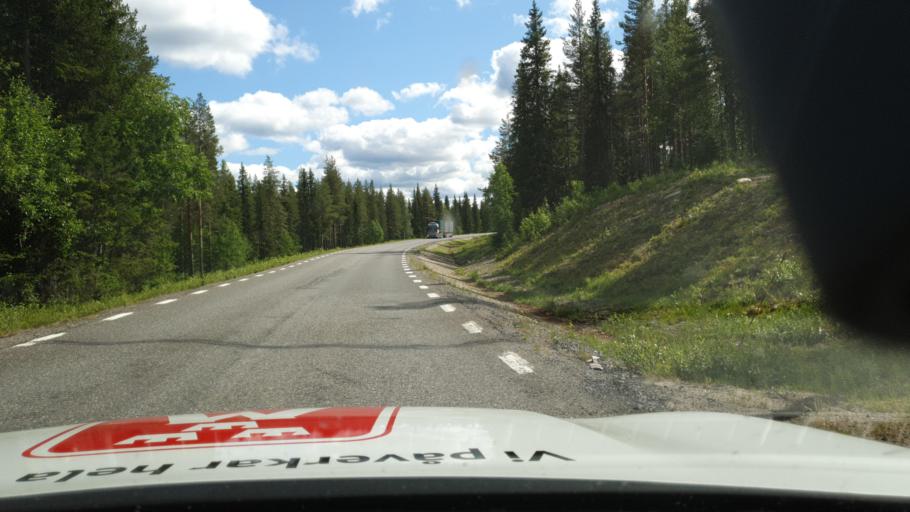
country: SE
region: Vaesterbotten
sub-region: Mala Kommun
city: Mala
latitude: 65.5109
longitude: 18.2776
